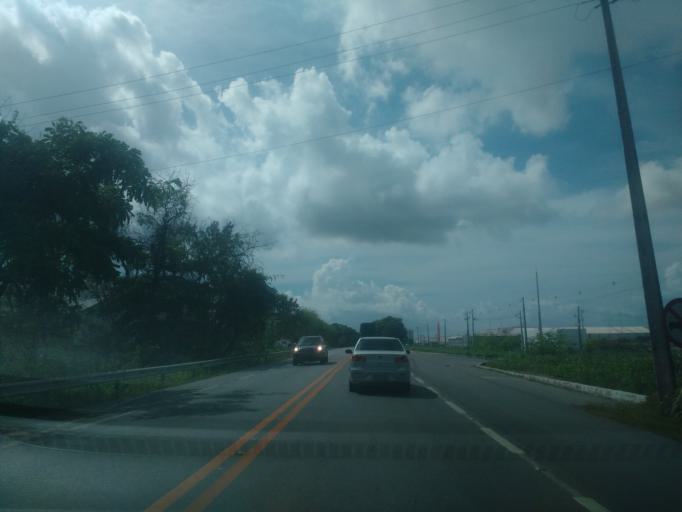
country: BR
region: Alagoas
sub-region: Marechal Deodoro
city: Marechal Deodoro
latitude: -9.6797
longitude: -35.8319
